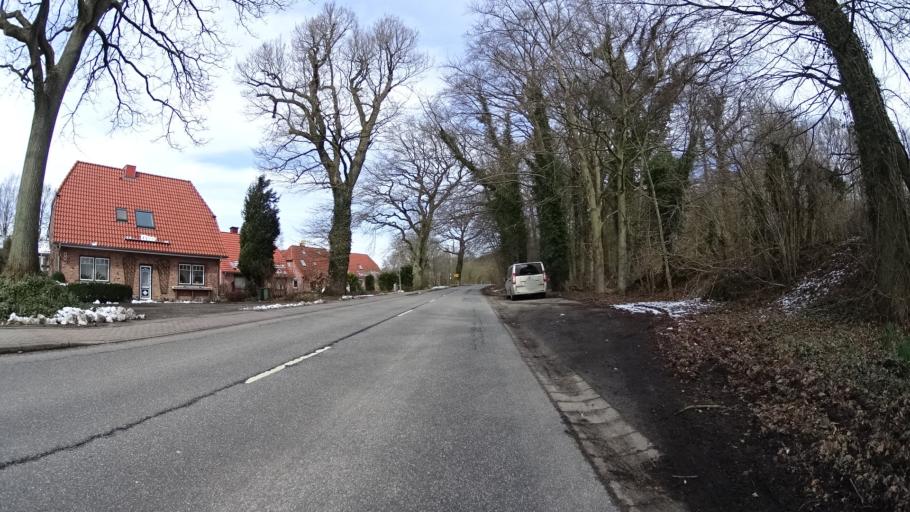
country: DE
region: Schleswig-Holstein
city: Kuhren
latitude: 54.2039
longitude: 10.2612
